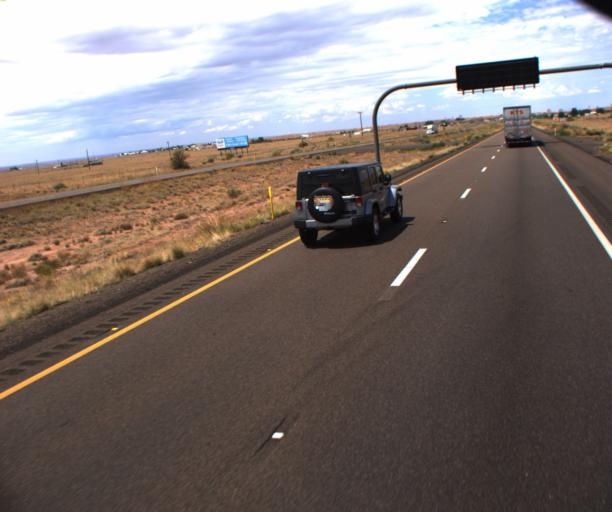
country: US
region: Arizona
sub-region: Navajo County
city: Holbrook
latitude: 34.9824
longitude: -110.0462
